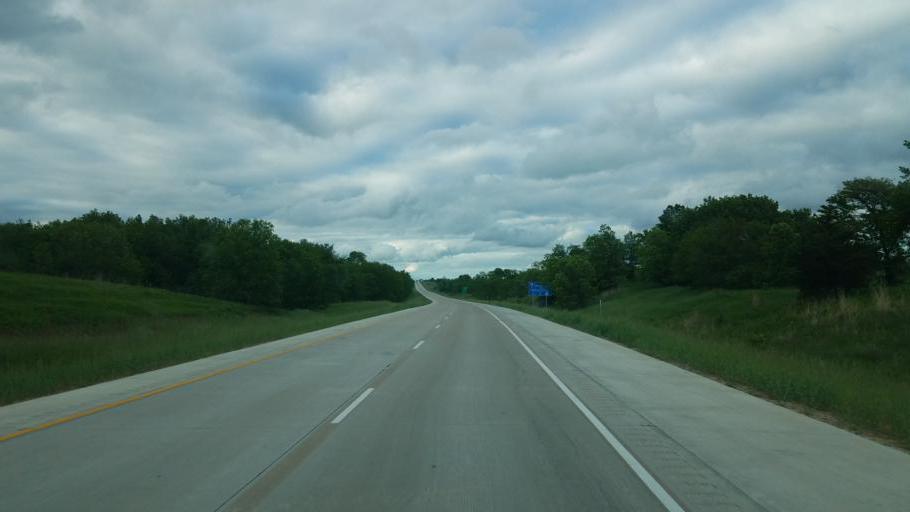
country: US
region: Iowa
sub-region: Decatur County
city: Lamoni
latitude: 40.6025
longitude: -93.9059
